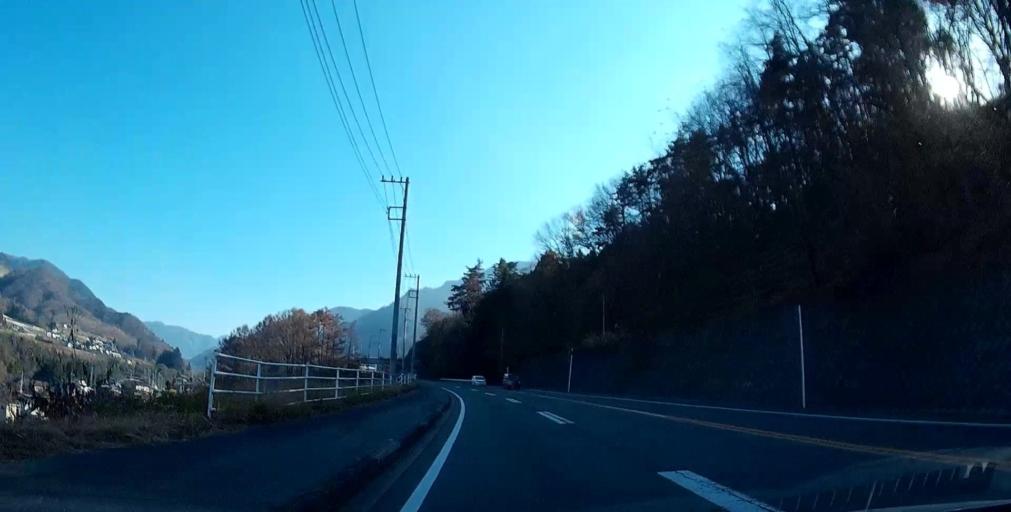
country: JP
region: Yamanashi
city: Isawa
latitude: 35.5997
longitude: 138.7089
